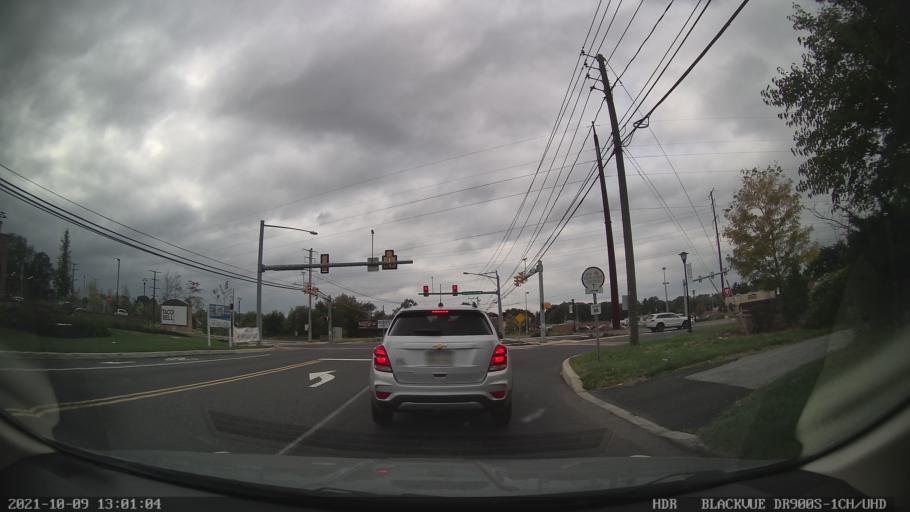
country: US
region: Pennsylvania
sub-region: Lehigh County
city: Wescosville
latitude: 40.5630
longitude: -75.5617
